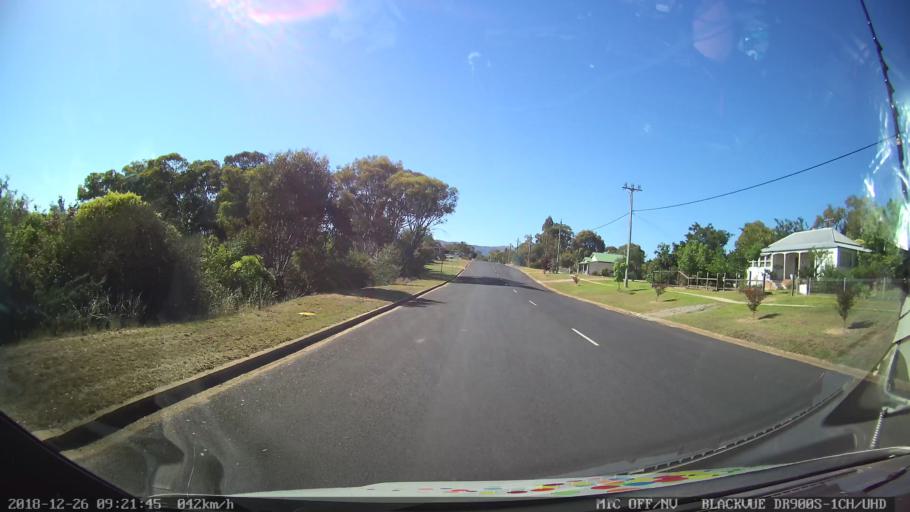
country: AU
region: New South Wales
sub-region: Mid-Western Regional
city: Kandos
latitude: -32.8022
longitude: 149.9741
